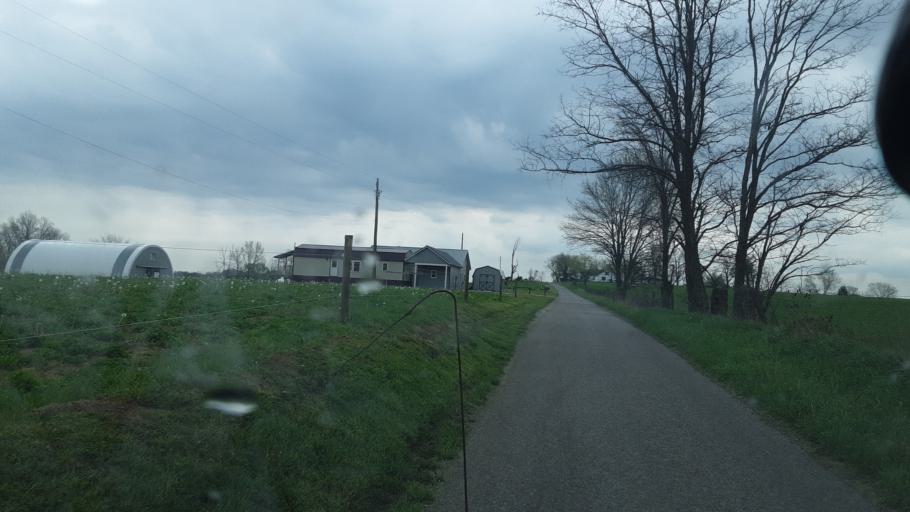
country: US
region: Kentucky
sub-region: Owen County
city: Owenton
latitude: 38.6087
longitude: -84.7688
